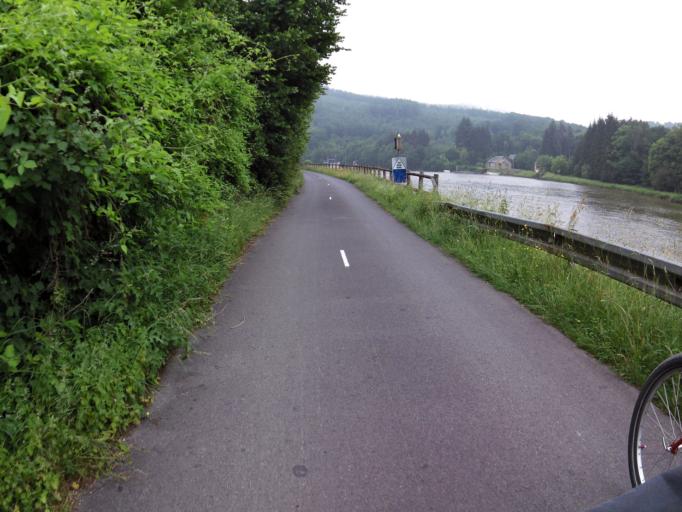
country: FR
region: Champagne-Ardenne
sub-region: Departement des Ardennes
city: Fumay
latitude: 49.9872
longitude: 4.7037
